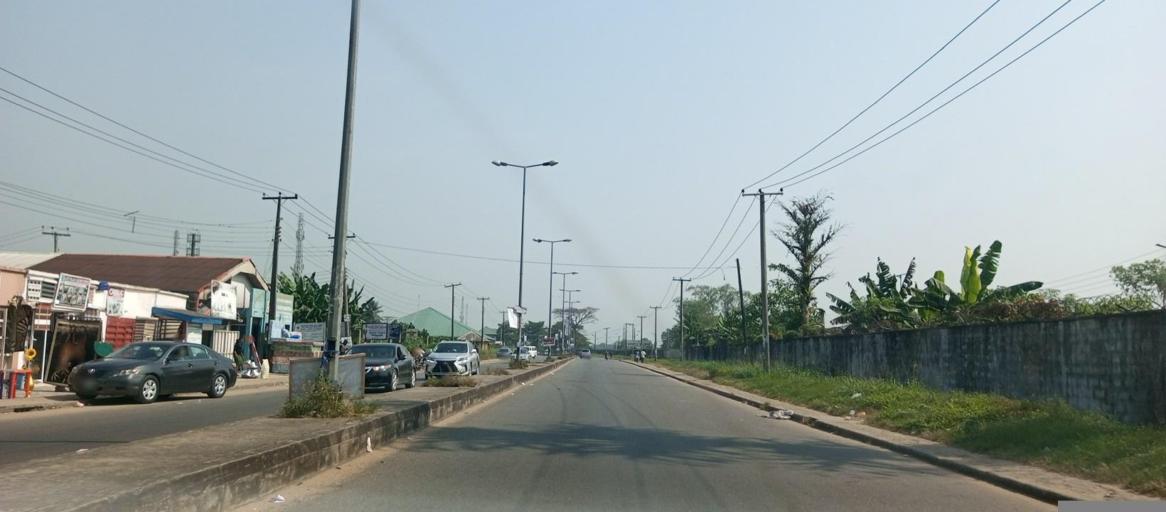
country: NG
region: Rivers
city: Emuoha
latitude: 4.8929
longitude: 6.9066
